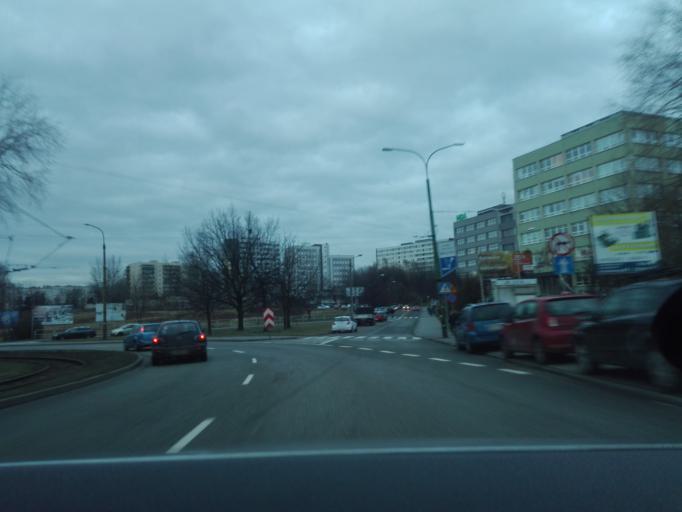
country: PL
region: Silesian Voivodeship
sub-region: Katowice
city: Katowice
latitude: 50.2735
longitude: 19.0253
